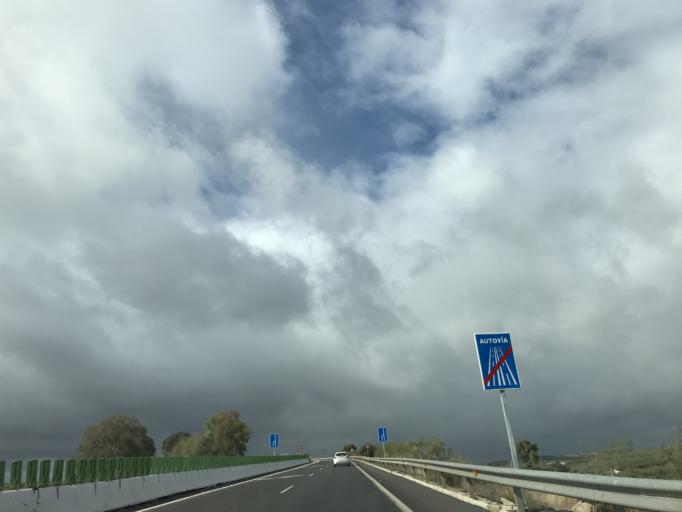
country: ES
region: Andalusia
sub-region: Provincia de Jaen
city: Bailen
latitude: 38.0988
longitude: -3.7361
